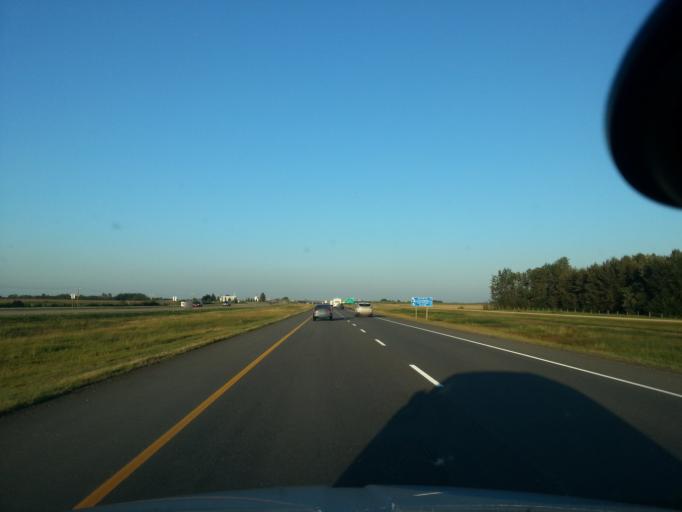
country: CA
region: Alberta
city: Stony Plain
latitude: 53.5694
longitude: -114.0183
